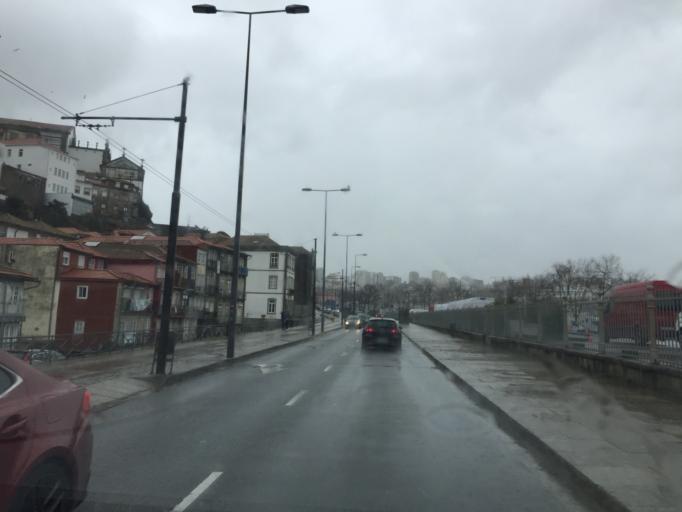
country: PT
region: Porto
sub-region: Vila Nova de Gaia
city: Vila Nova de Gaia
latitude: 41.1424
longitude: -8.6200
